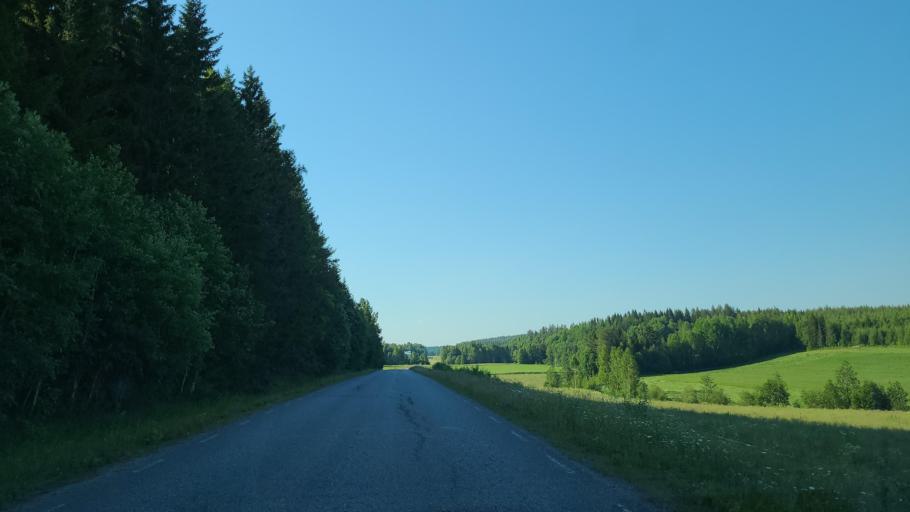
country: SE
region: Vaesterbotten
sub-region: Robertsfors Kommun
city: Robertsfors
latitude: 64.2768
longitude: 20.8063
